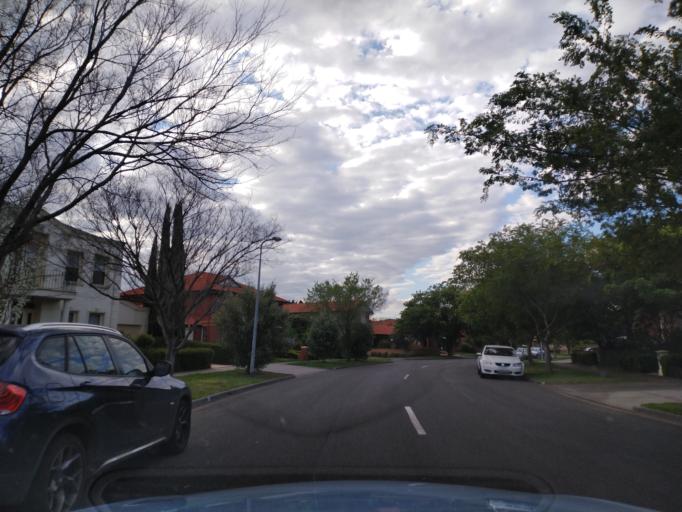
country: AU
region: Victoria
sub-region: Hobsons Bay
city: Williamstown North
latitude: -37.8586
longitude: 144.8787
